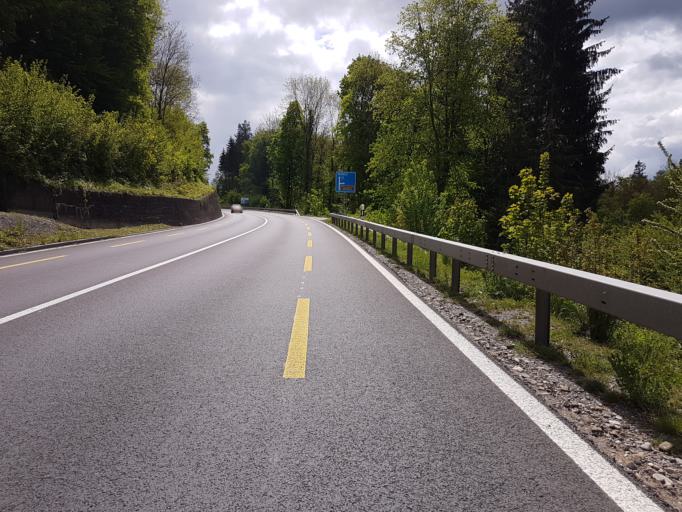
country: CH
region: Aargau
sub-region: Bezirk Brugg
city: Schinznach Bad
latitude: 47.4611
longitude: 8.1706
